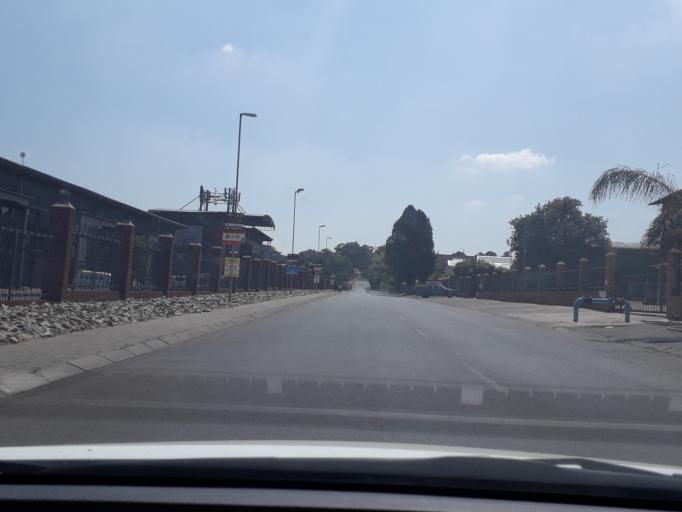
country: ZA
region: Gauteng
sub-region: West Rand District Municipality
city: Muldersdriseloop
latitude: -26.0786
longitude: 27.9154
